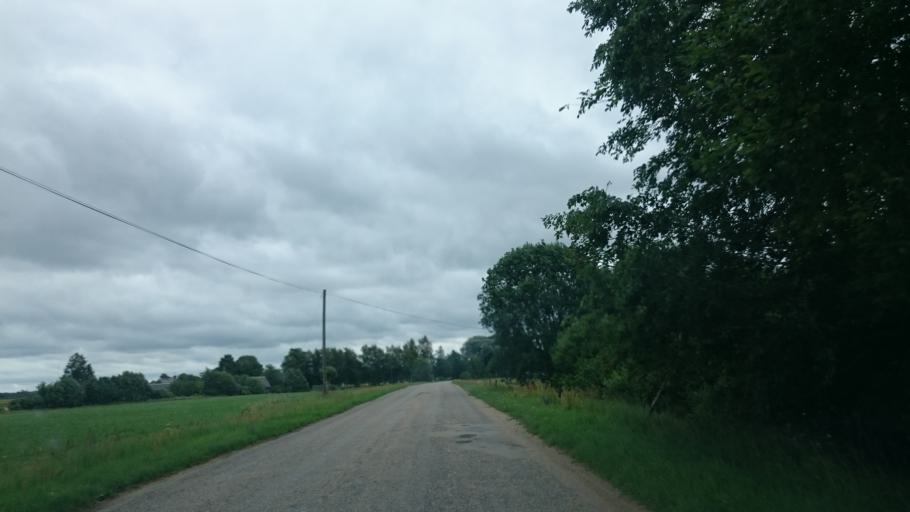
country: LV
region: Durbe
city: Liegi
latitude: 56.7434
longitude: 21.3739
